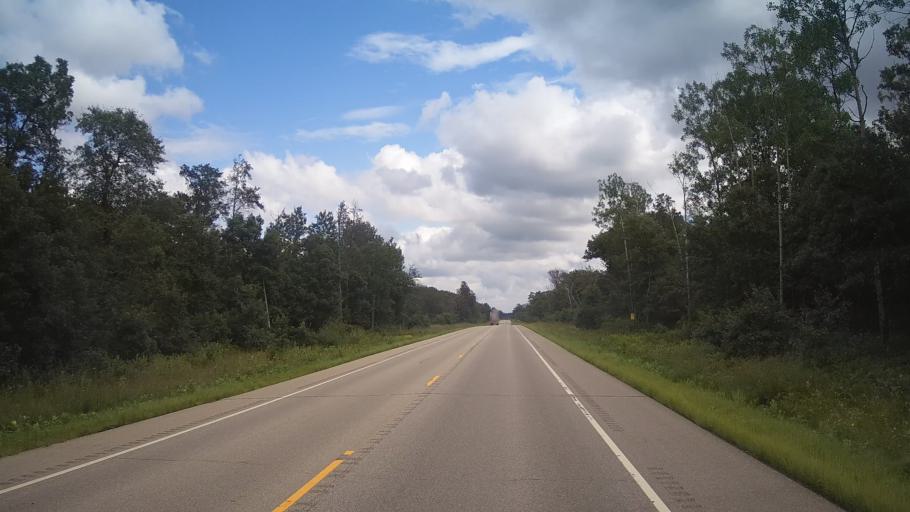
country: US
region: Wisconsin
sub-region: Adams County
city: Friendship
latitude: 44.0254
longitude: -89.7153
